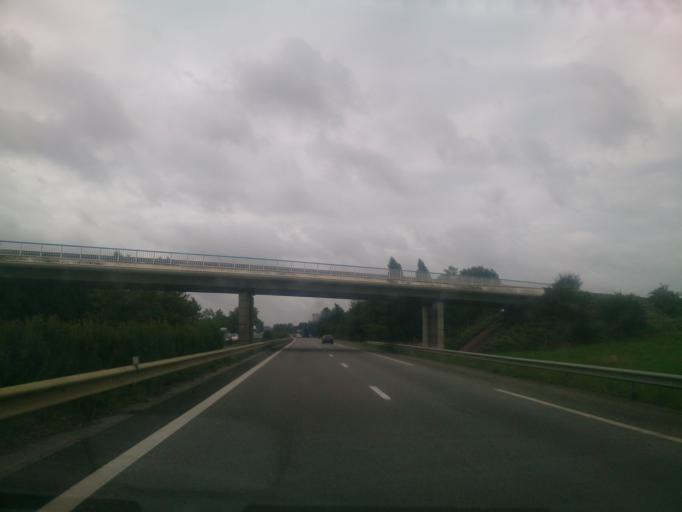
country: FR
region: Midi-Pyrenees
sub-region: Departement de la Haute-Garonne
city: Noe
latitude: 43.3691
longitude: 1.2748
